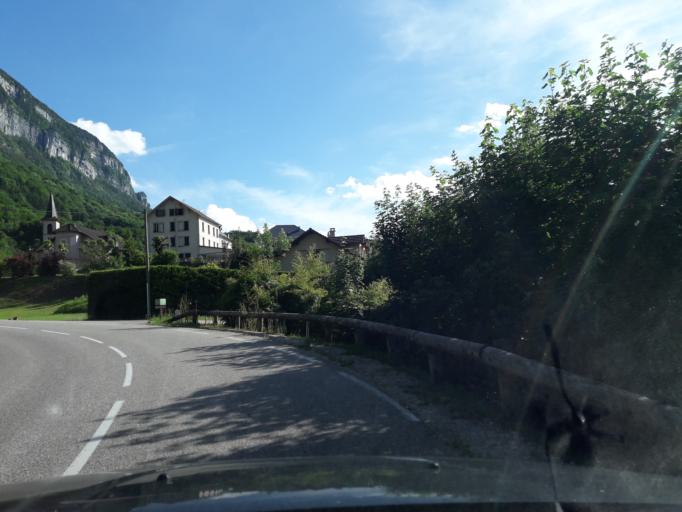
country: FR
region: Rhone-Alpes
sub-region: Departement de la Savoie
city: Vimines
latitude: 45.5390
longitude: 5.8155
